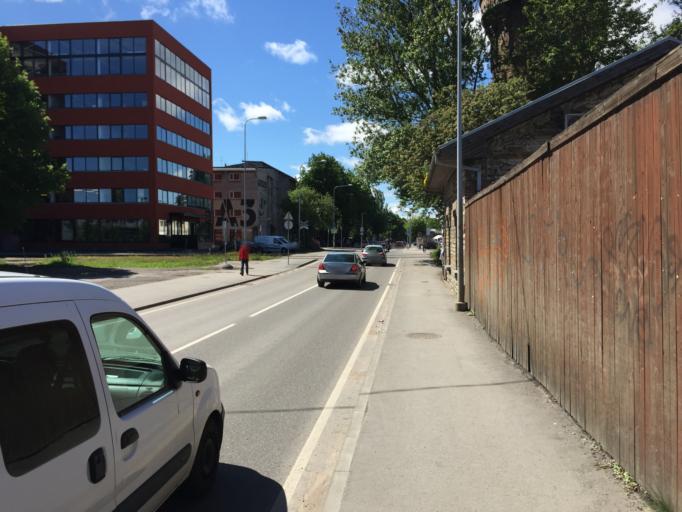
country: EE
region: Harju
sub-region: Tallinna linn
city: Tallinn
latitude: 59.4409
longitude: 24.7302
